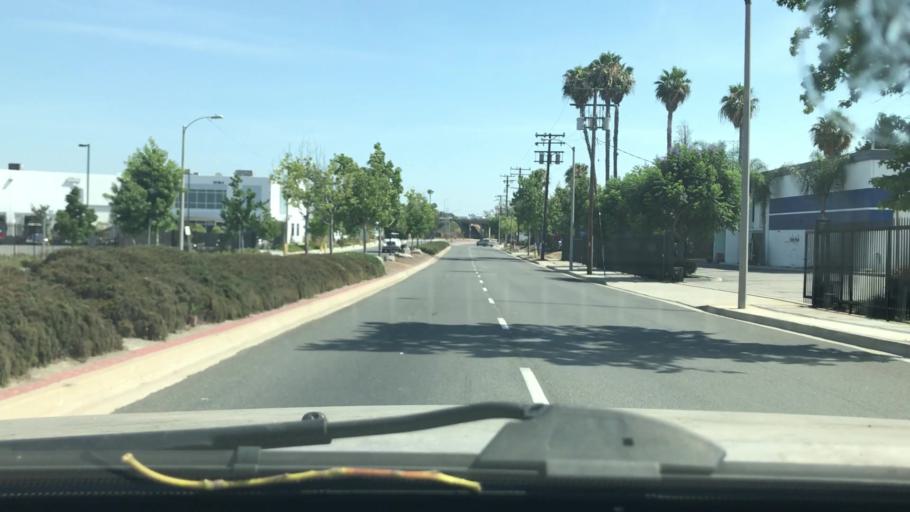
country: US
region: California
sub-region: Los Angeles County
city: Carson
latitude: 33.8580
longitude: -118.2816
